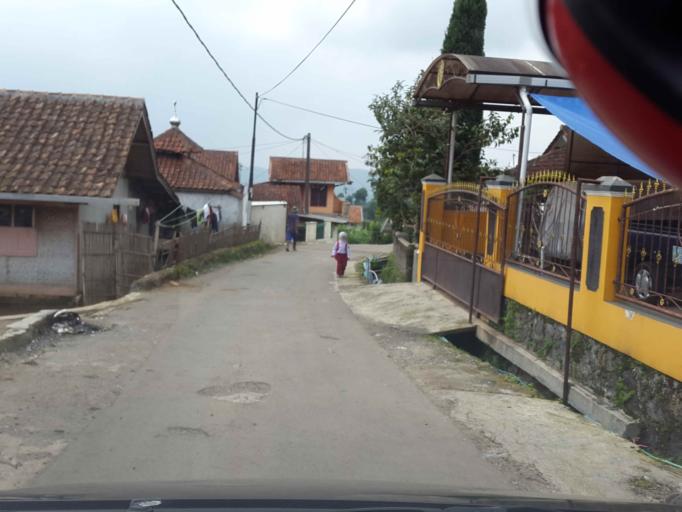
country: ID
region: West Java
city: Lembang
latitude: -6.7913
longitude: 107.6498
